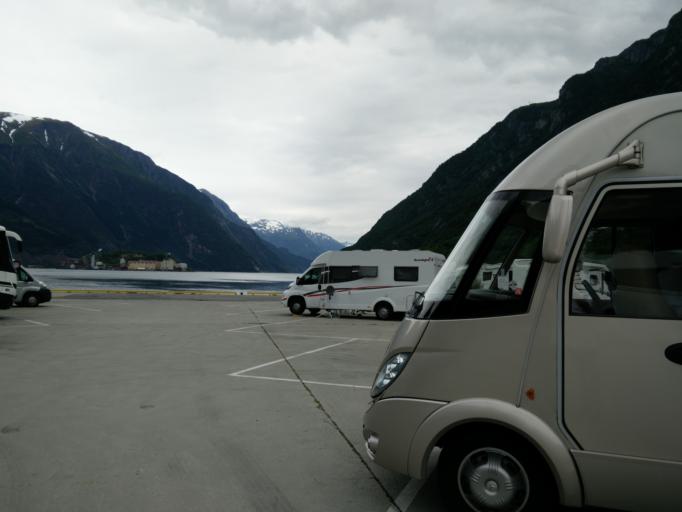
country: NO
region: Hordaland
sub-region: Odda
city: Odda
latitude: 60.0714
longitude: 6.5488
